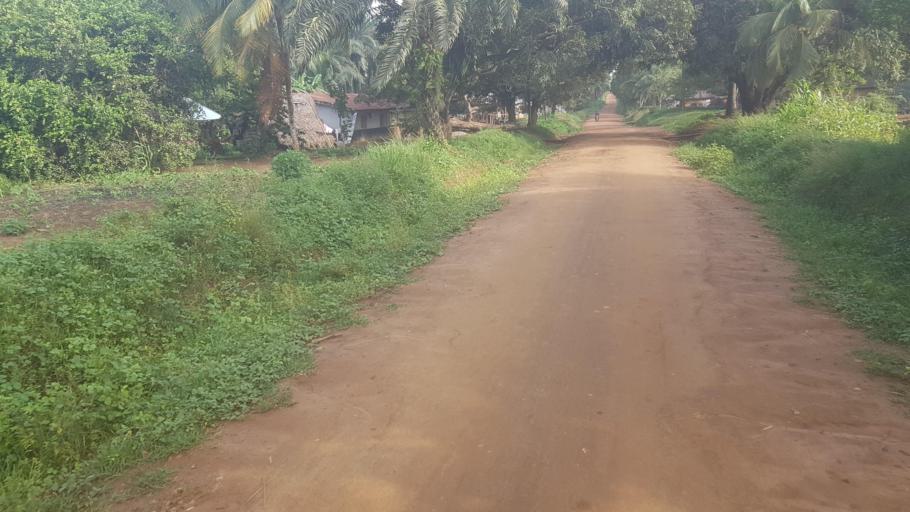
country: SL
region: Southern Province
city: Sumbuya
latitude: 7.6129
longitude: -12.1423
